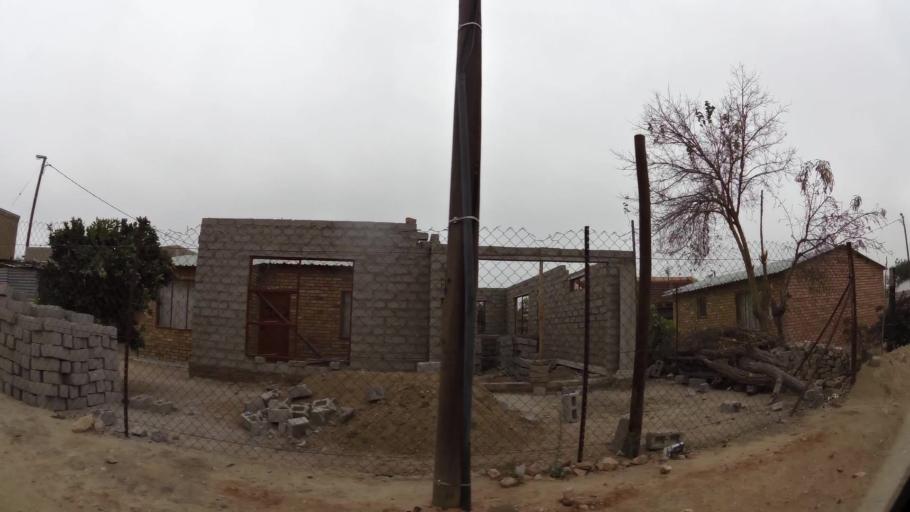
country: ZA
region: Limpopo
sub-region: Capricorn District Municipality
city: Polokwane
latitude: -23.8346
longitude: 29.3914
